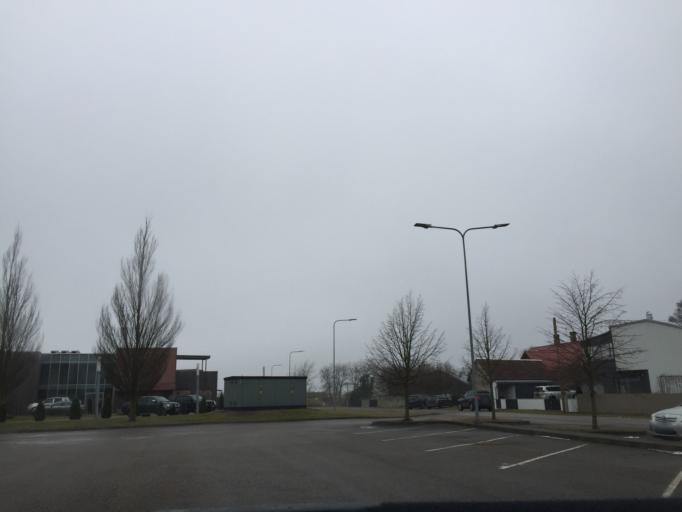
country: EE
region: Saare
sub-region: Kuressaare linn
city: Kuressaare
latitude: 58.2466
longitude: 22.4699
